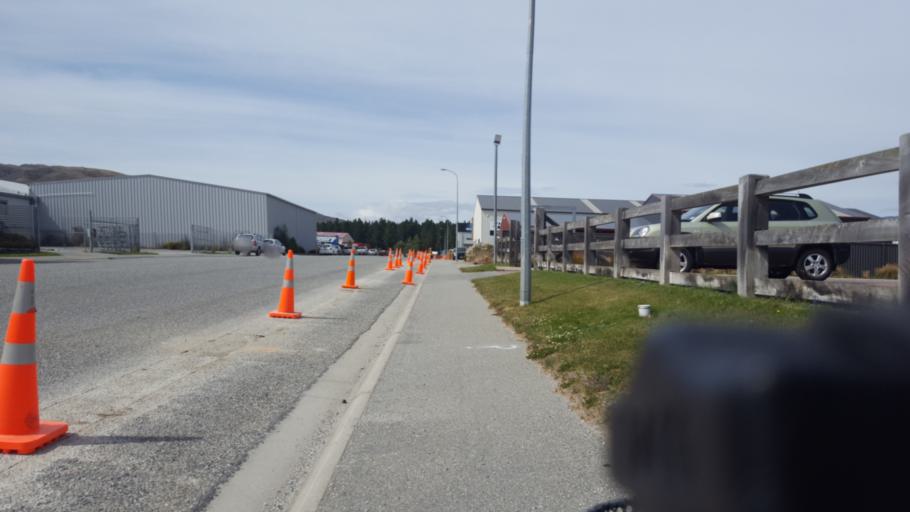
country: NZ
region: Otago
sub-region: Queenstown-Lakes District
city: Wanaka
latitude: -45.0501
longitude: 169.1878
